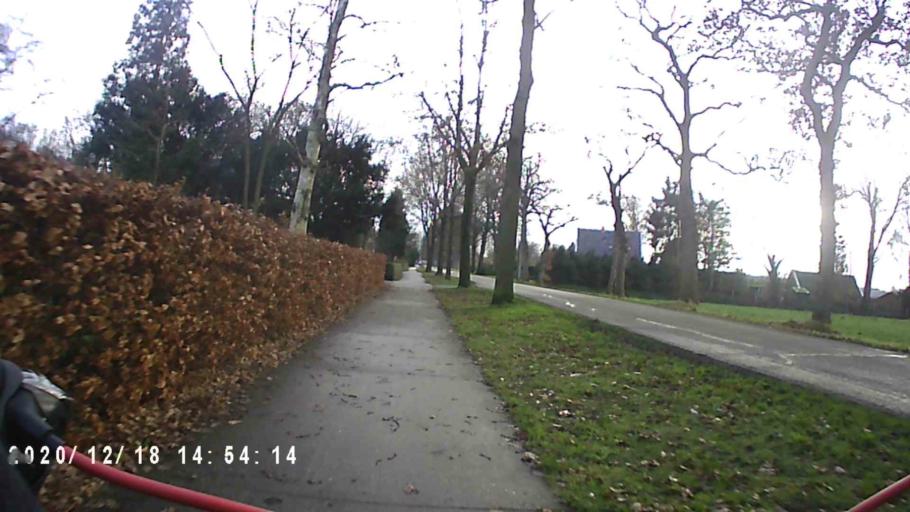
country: NL
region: Groningen
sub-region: Gemeente Haren
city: Haren
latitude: 53.1885
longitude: 6.6818
